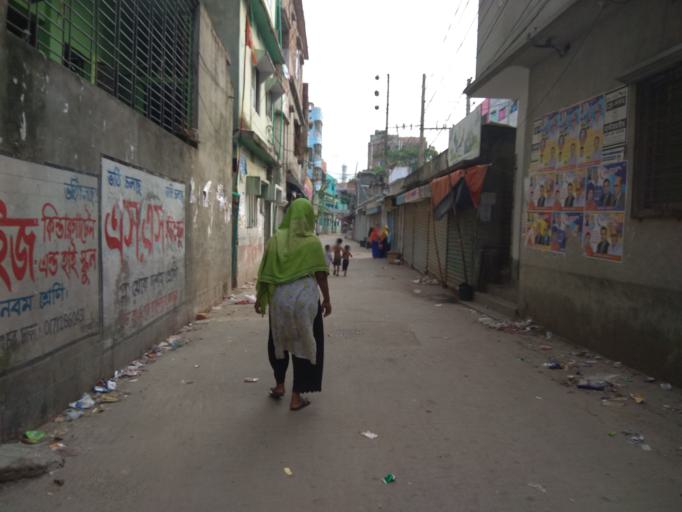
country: BD
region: Dhaka
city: Azimpur
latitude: 23.7194
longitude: 90.3760
